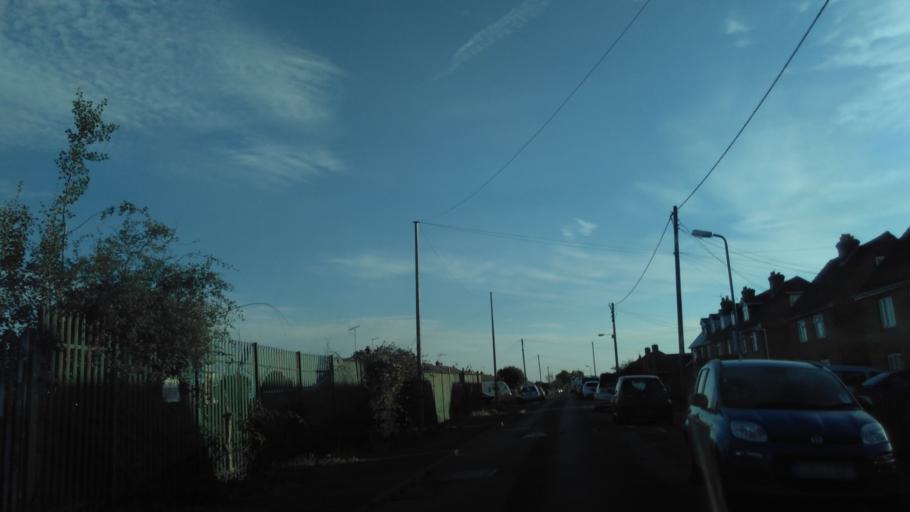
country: GB
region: England
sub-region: Kent
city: Dunkirk
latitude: 51.2926
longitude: 0.9799
